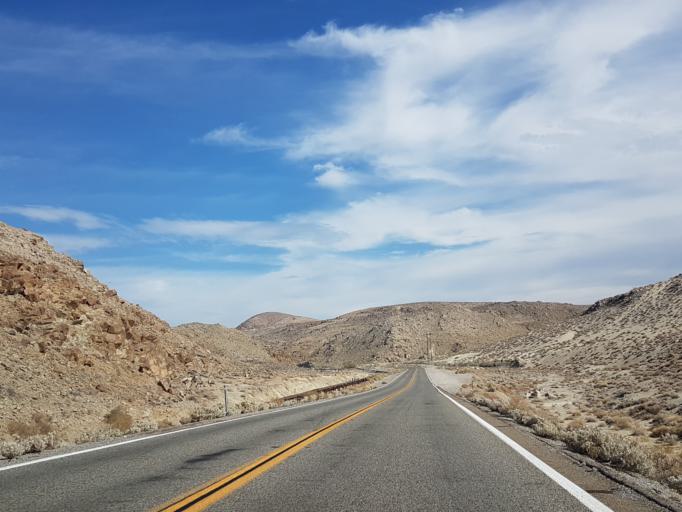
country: US
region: California
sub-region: San Bernardino County
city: Searles Valley
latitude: 35.6558
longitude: -117.4526
